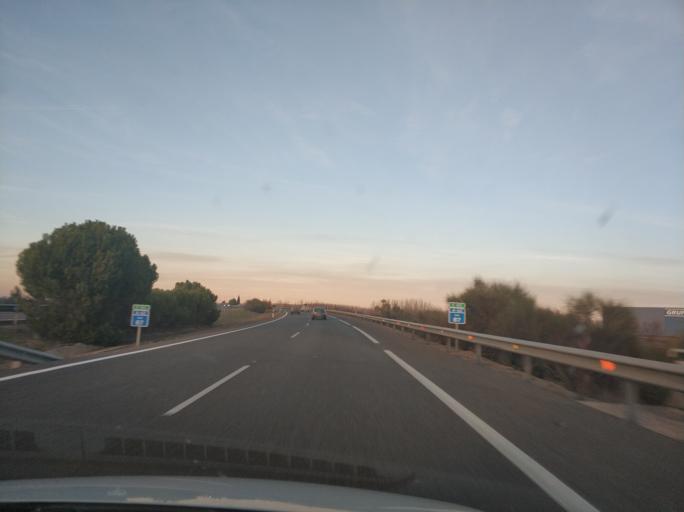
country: ES
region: Castille and Leon
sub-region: Provincia de Palencia
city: Venta de Banos
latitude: 41.9274
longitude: -4.4995
